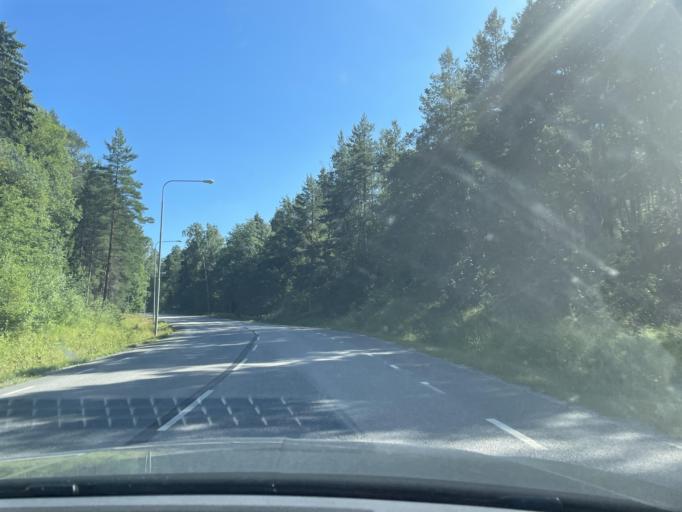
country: SE
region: Stockholm
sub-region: Sigtuna Kommun
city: Marsta
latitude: 59.6209
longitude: 17.8177
